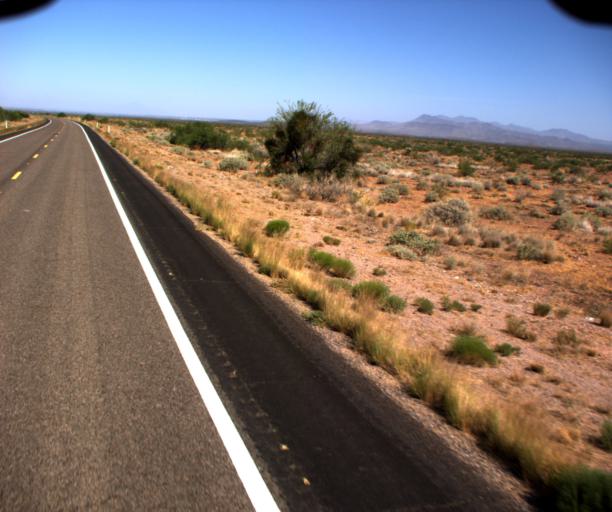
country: US
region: Arizona
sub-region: Graham County
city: Swift Trail Junction
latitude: 32.7642
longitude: -109.4516
